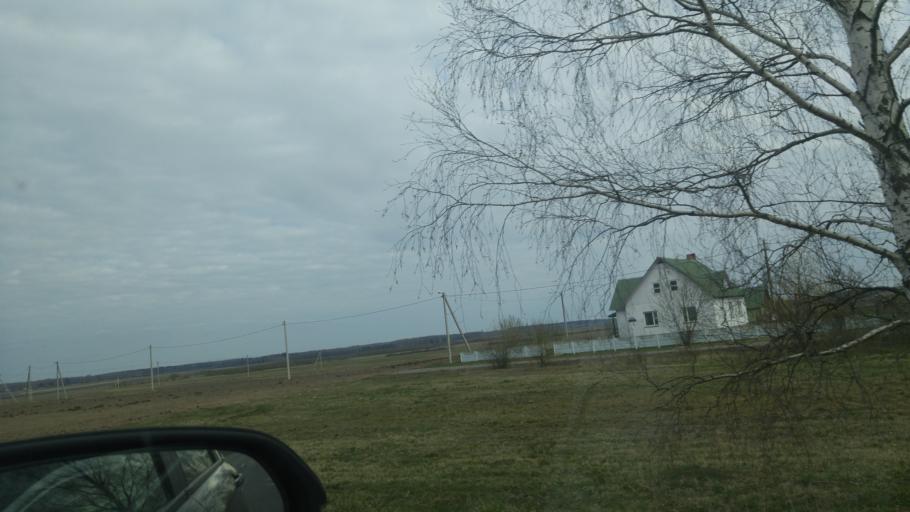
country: BY
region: Minsk
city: Chervyen'
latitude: 53.6156
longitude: 28.6951
